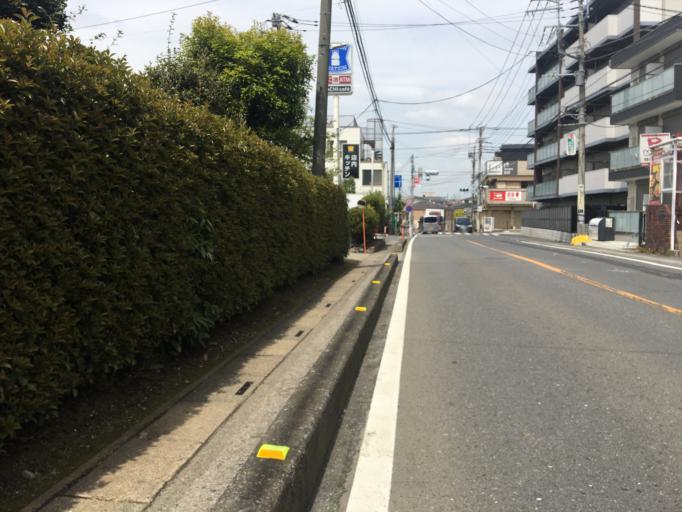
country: JP
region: Saitama
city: Oi
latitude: 35.8457
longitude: 139.5433
